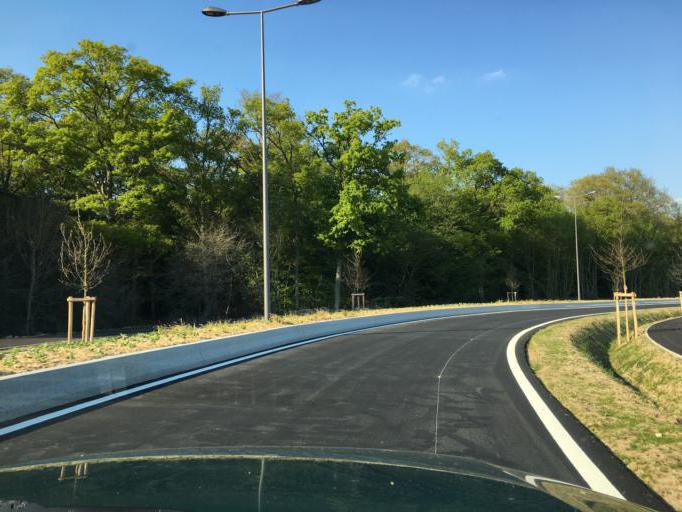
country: FR
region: Centre
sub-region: Departement du Loiret
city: Gidy
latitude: 47.9700
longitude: 1.8473
